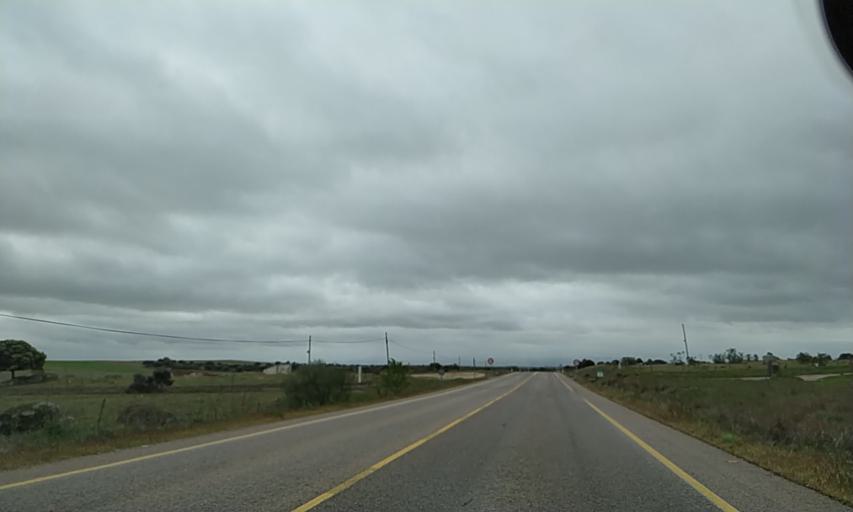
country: ES
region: Extremadura
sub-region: Provincia de Caceres
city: Caceres
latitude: 39.4244
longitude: -6.4114
